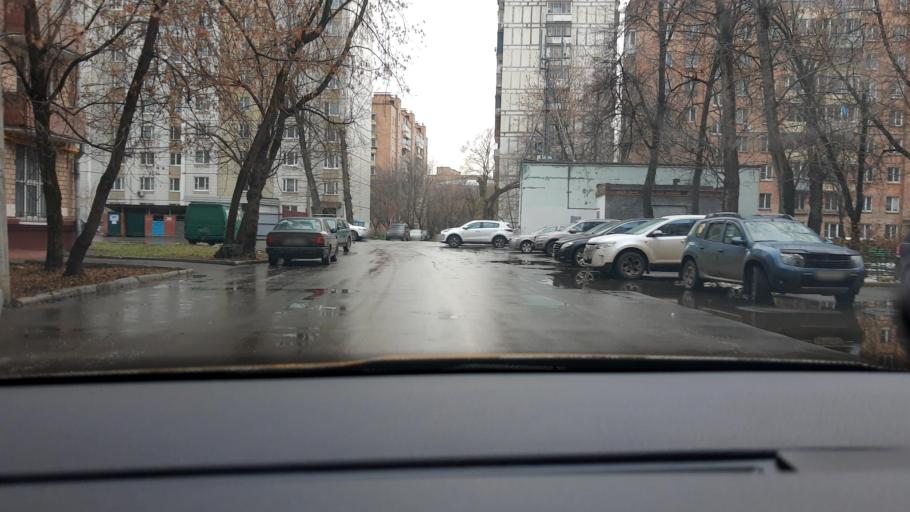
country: RU
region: Moscow
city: Ryazanskiy
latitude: 55.7357
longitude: 37.7489
